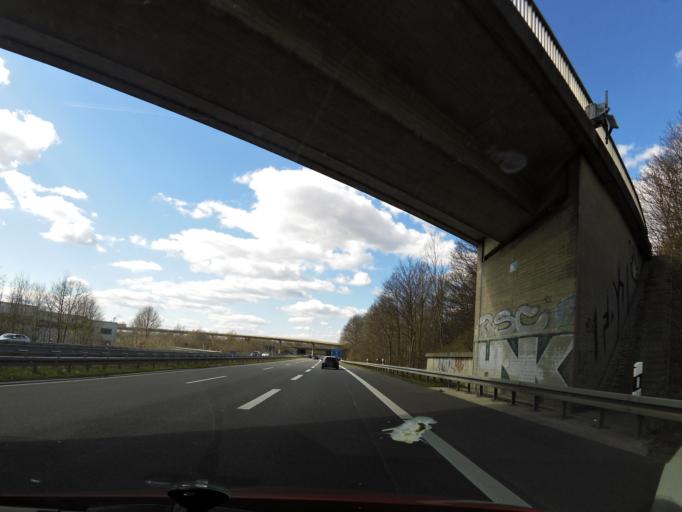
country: DE
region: Lower Saxony
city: Braunschweig
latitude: 52.2830
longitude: 10.4966
